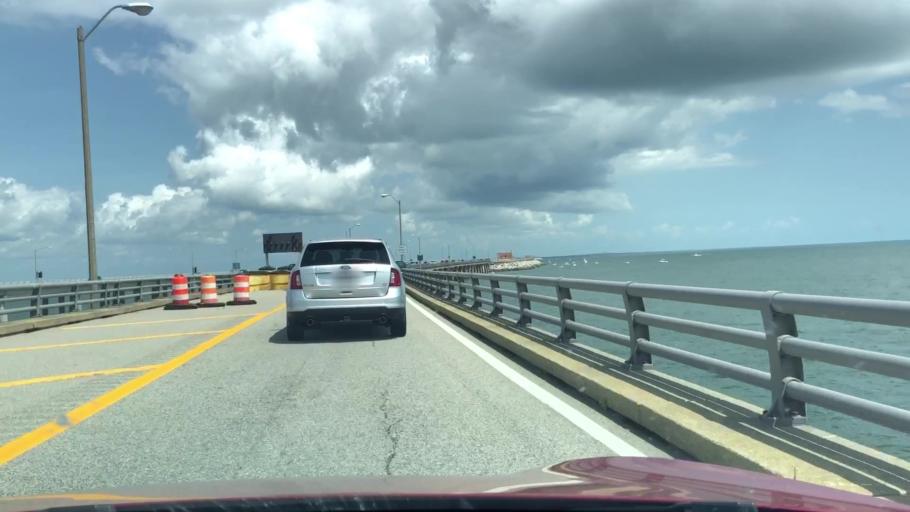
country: US
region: Virginia
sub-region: City of Virginia Beach
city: Virginia Beach
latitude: 37.0302
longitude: -76.0848
